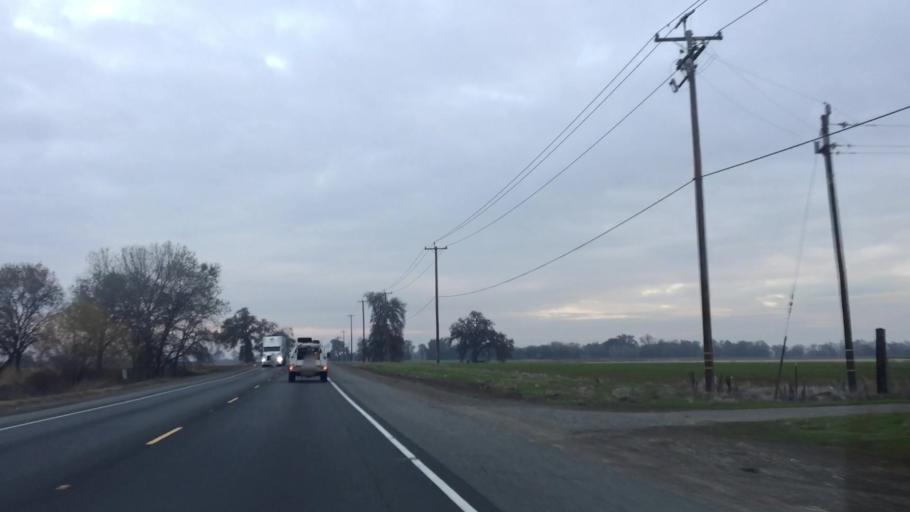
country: US
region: California
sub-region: Sutter County
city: Live Oak
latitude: 39.3281
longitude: -121.5970
